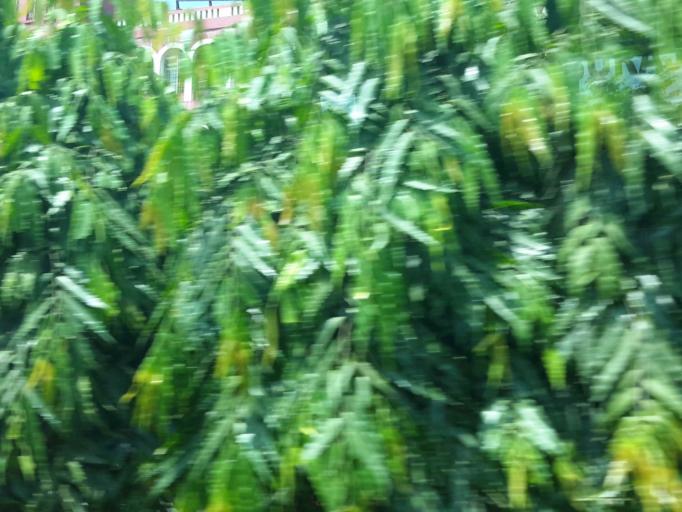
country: IN
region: West Bengal
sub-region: Kolkata
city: Bara Bazar
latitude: 22.5815
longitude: 88.3426
